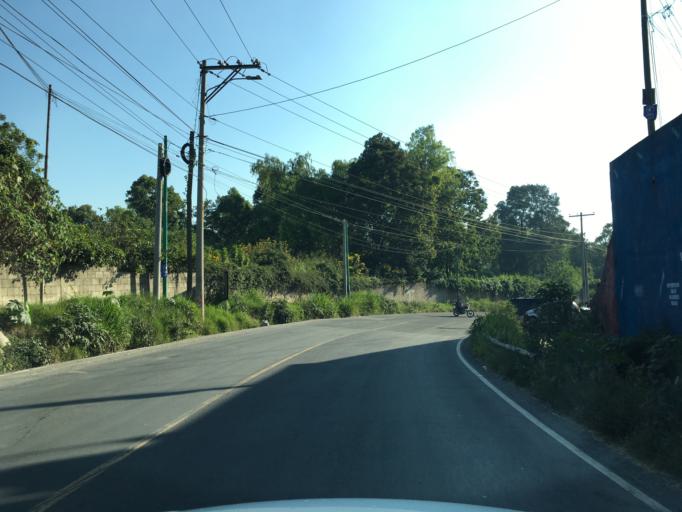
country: GT
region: Guatemala
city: Villa Nueva
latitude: 14.5368
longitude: -90.6149
